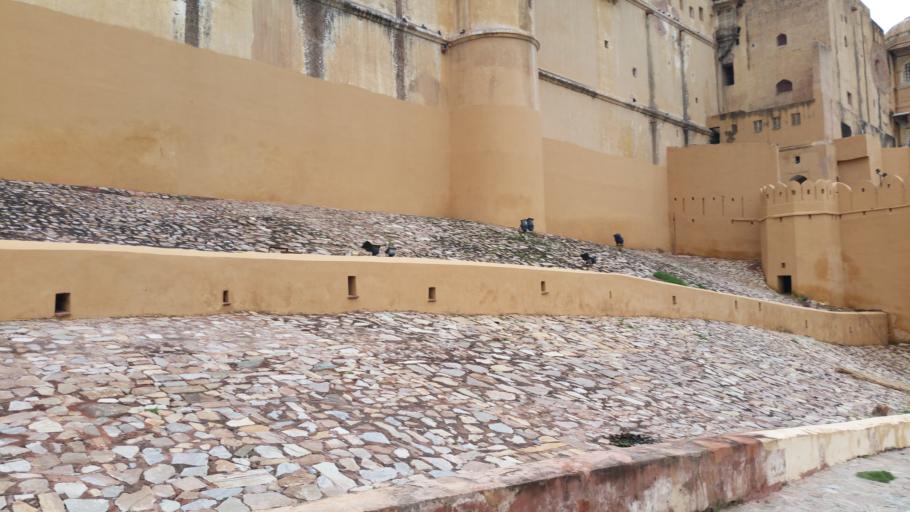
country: IN
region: Rajasthan
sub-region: Jaipur
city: Jaipur
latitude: 26.9849
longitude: 75.8503
